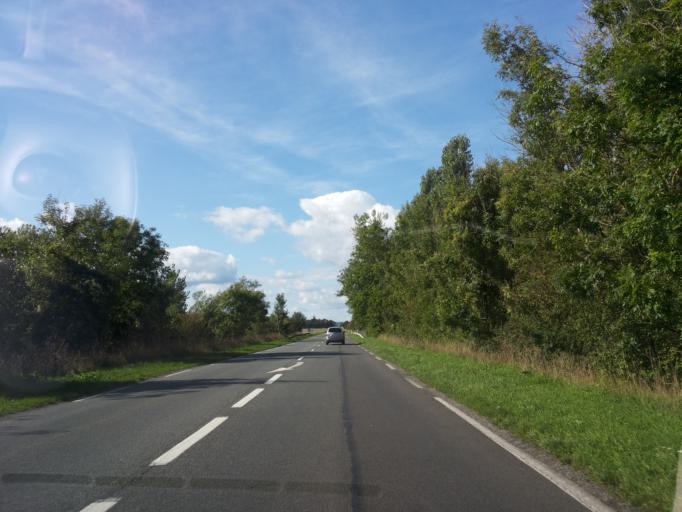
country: FR
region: Champagne-Ardenne
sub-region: Departement de la Marne
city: Cormicy
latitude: 49.4150
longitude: 3.8840
